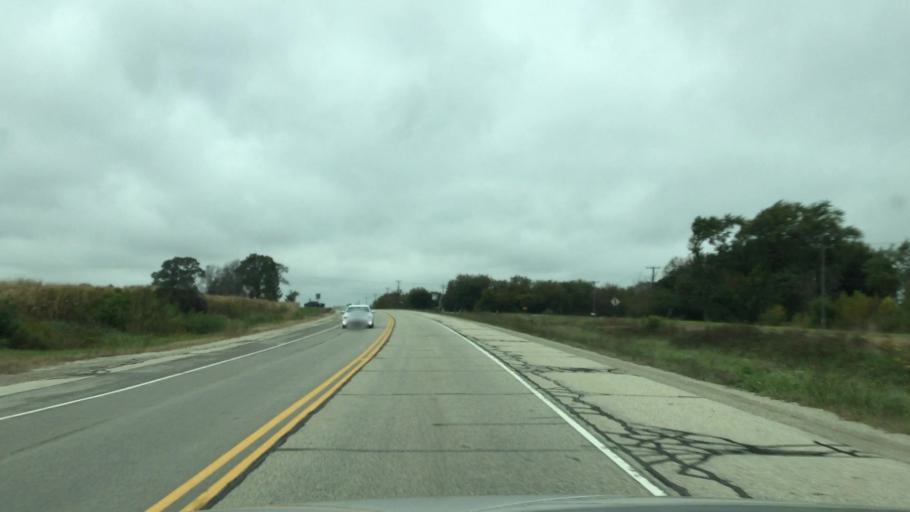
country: US
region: Wisconsin
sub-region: Racine County
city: Franksville
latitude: 42.7325
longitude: -87.9849
